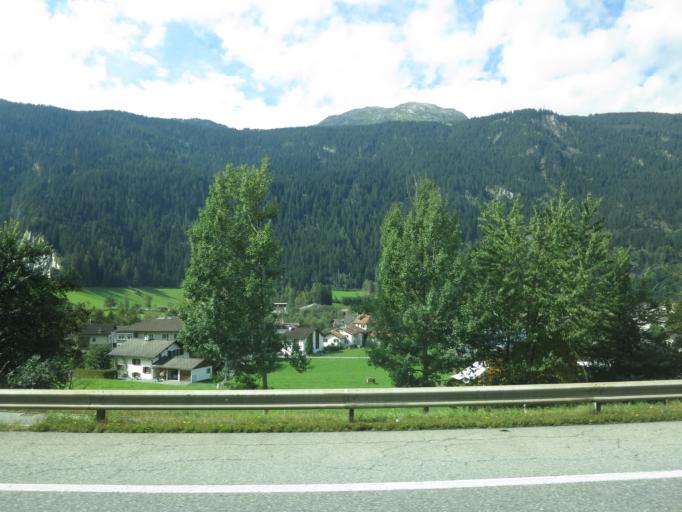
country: CH
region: Grisons
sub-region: Hinterrhein District
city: Thusis
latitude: 46.6000
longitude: 9.4312
